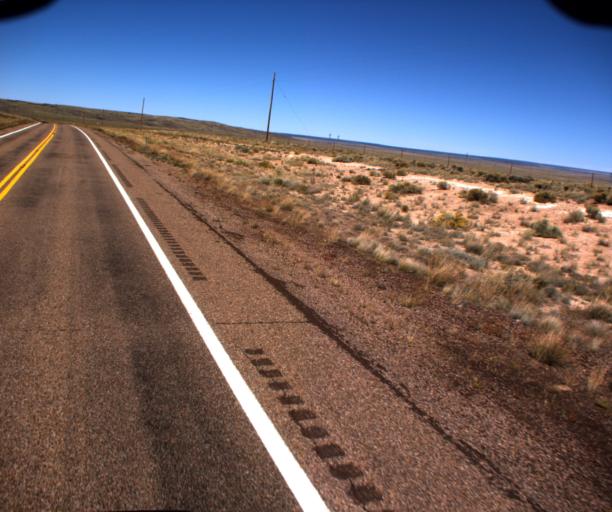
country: US
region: Arizona
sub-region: Apache County
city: Saint Johns
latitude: 34.5331
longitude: -109.4617
